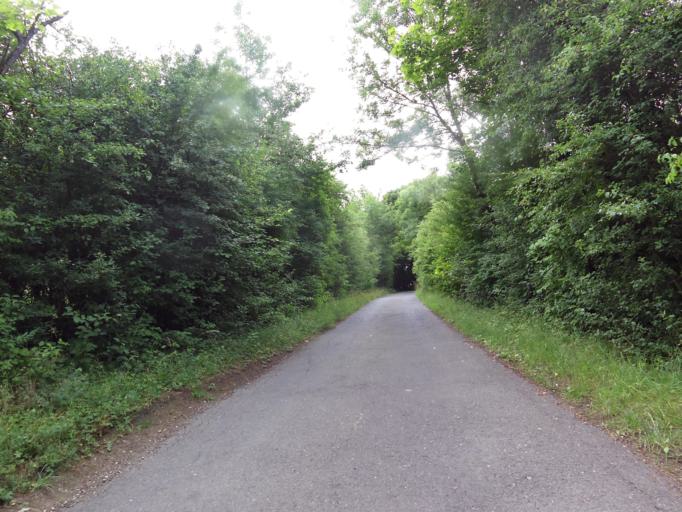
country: DE
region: Bavaria
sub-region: Regierungsbezirk Unterfranken
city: Wuerzburg
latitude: 49.8090
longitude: 9.9243
